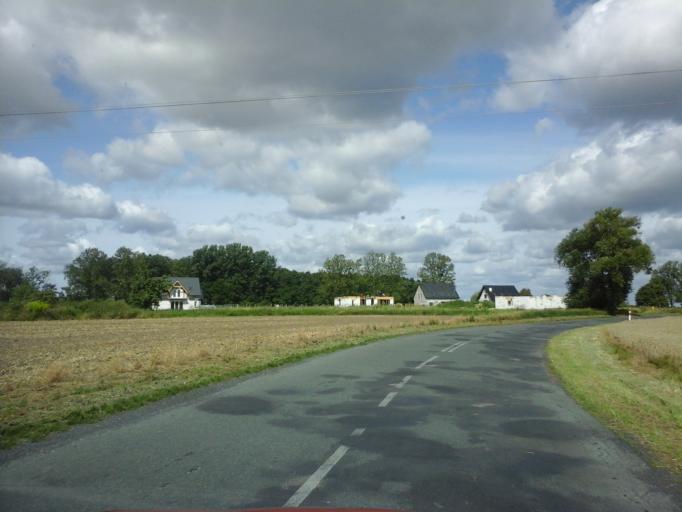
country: PL
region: West Pomeranian Voivodeship
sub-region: Powiat stargardzki
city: Kobylanka
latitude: 53.3177
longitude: 14.9316
